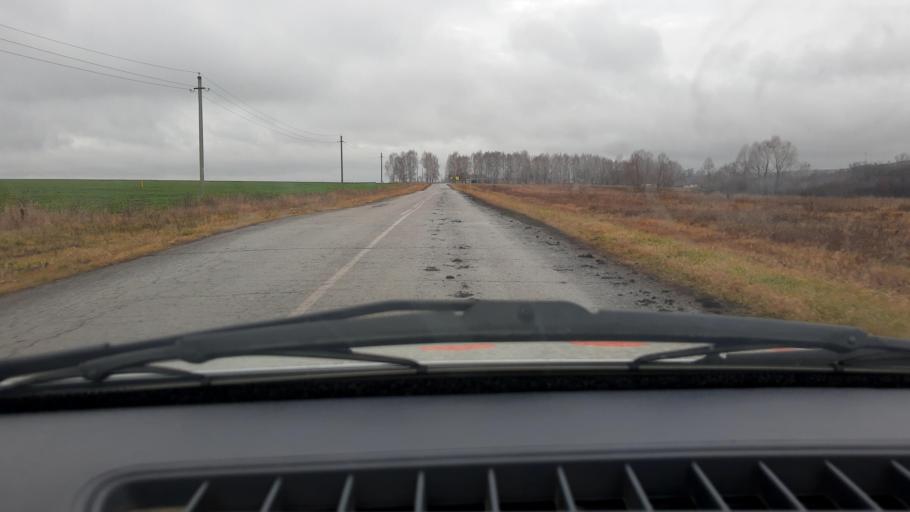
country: RU
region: Bashkortostan
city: Iglino
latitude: 54.7656
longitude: 56.3823
